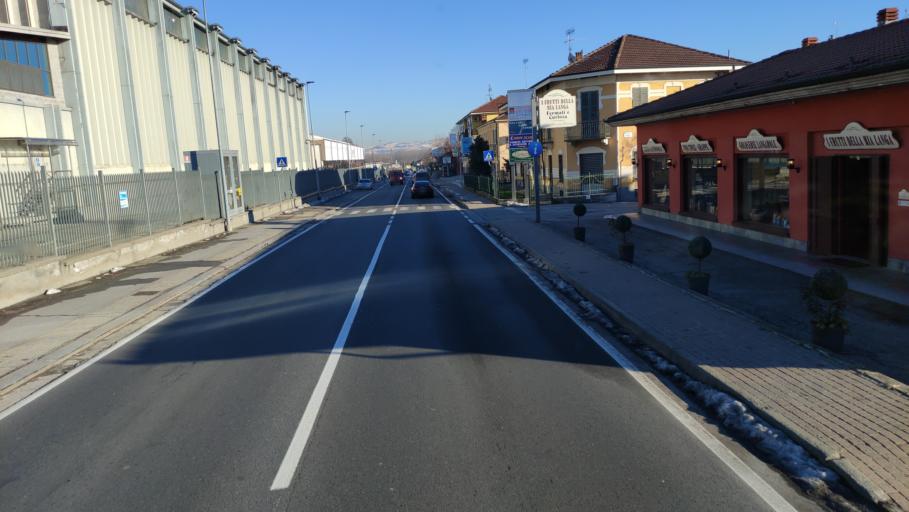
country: IT
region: Piedmont
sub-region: Provincia di Cuneo
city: Cinzano
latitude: 44.6932
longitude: 7.9221
